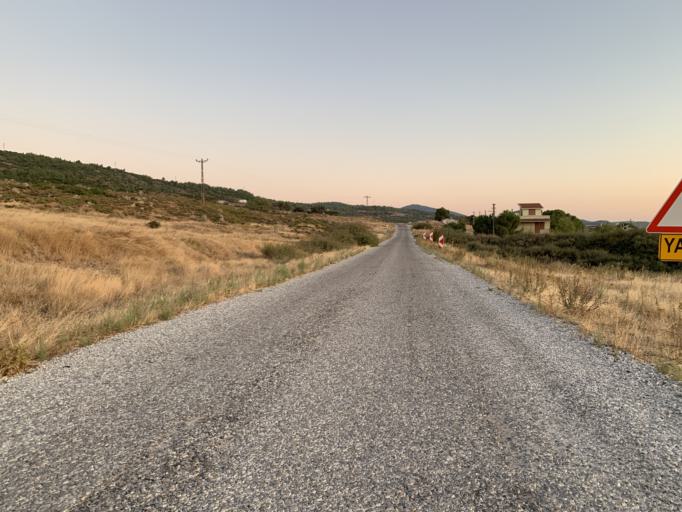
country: TR
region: Izmir
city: Uzunkuyu
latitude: 38.3263
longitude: 26.5837
